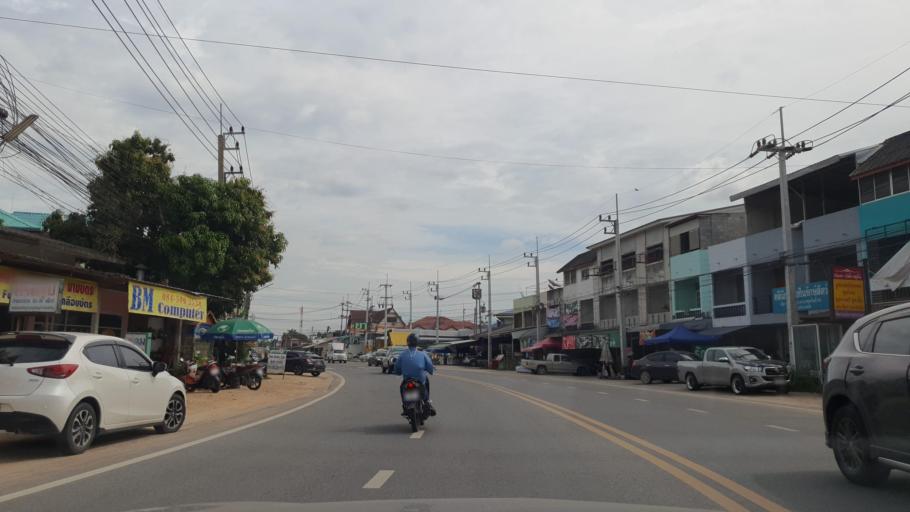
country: TH
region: Chon Buri
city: Phatthaya
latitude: 12.9448
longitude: 100.9384
